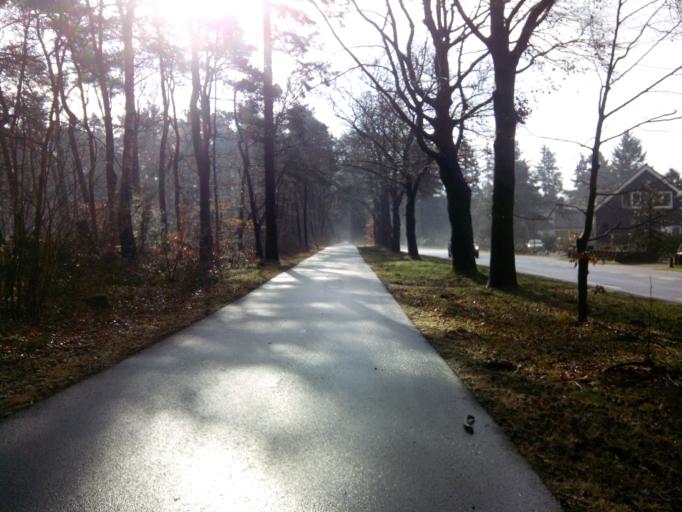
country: NL
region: Utrecht
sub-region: Gemeente Utrechtse Heuvelrug
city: Leersum
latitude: 52.0246
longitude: 5.4183
